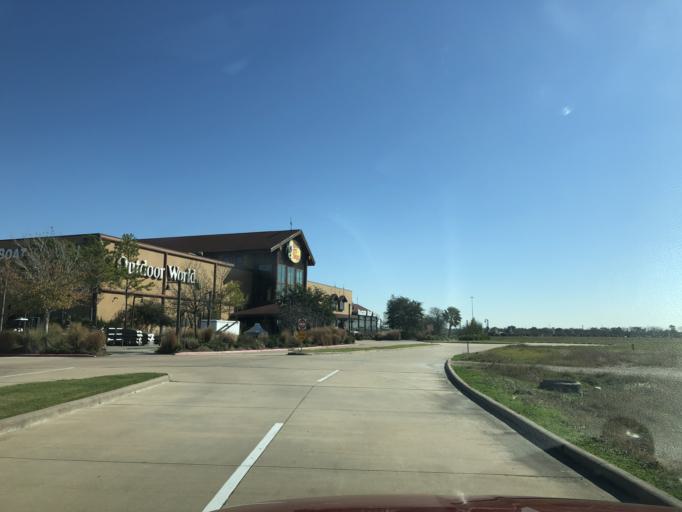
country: US
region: Texas
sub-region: Brazoria County
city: Brookside Village
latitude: 29.5951
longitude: -95.3911
